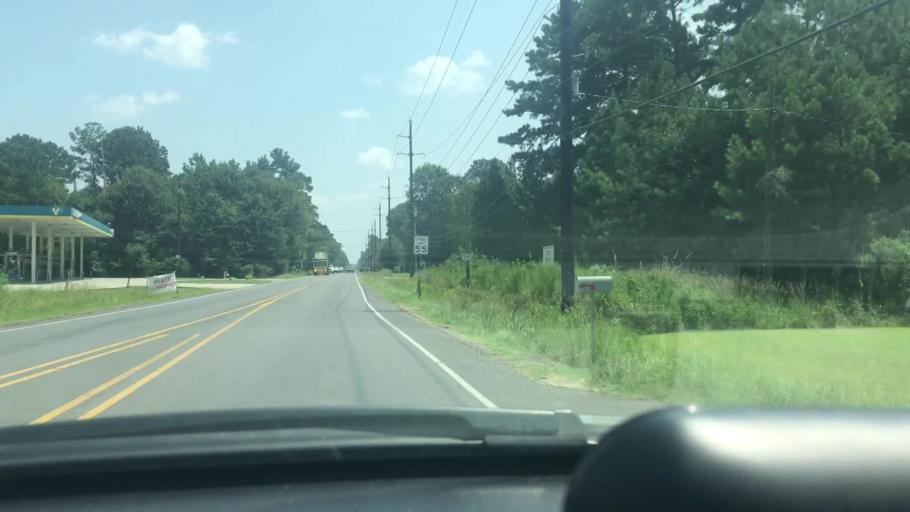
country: US
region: Louisiana
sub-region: Livingston Parish
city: Walker
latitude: 30.4838
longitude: -90.9049
